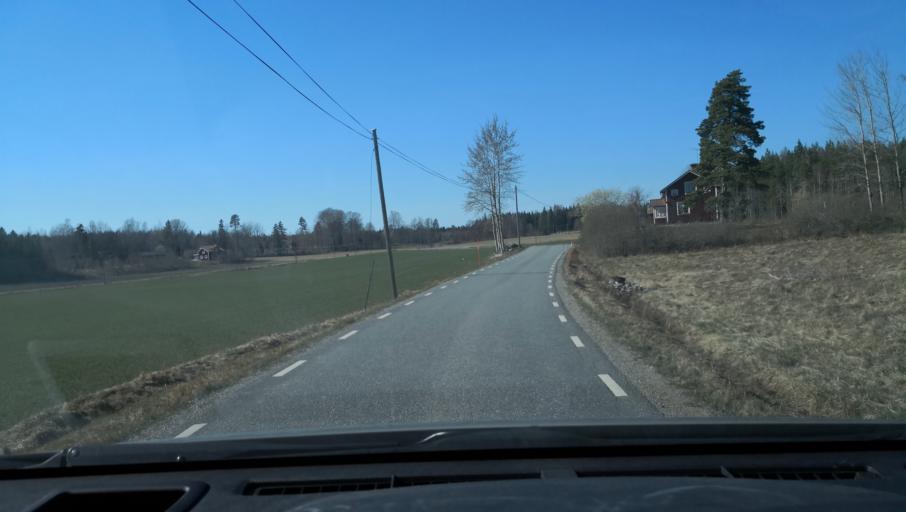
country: SE
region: Vaestmanland
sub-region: Sala Kommun
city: Sala
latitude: 59.9278
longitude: 16.4655
